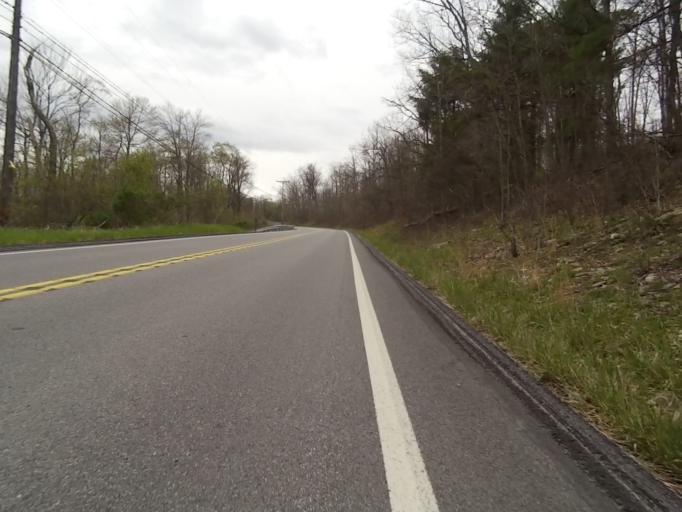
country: US
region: Pennsylvania
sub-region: Clearfield County
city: Troy
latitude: 40.9004
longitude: -78.1557
